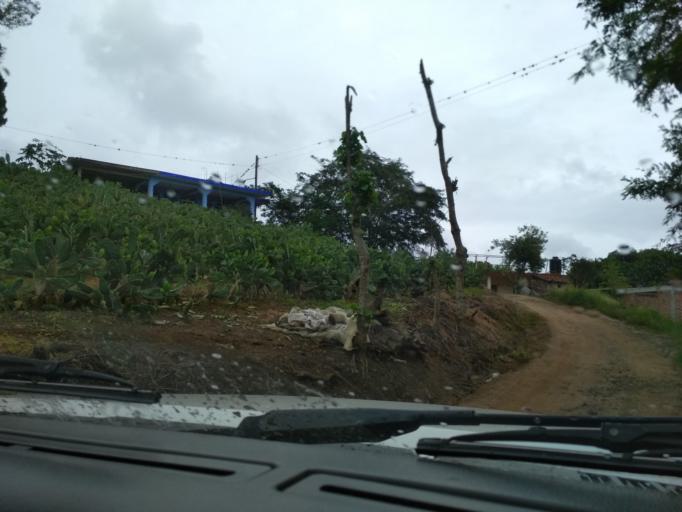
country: MX
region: Veracruz
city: El Castillo
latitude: 19.5363
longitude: -96.8156
